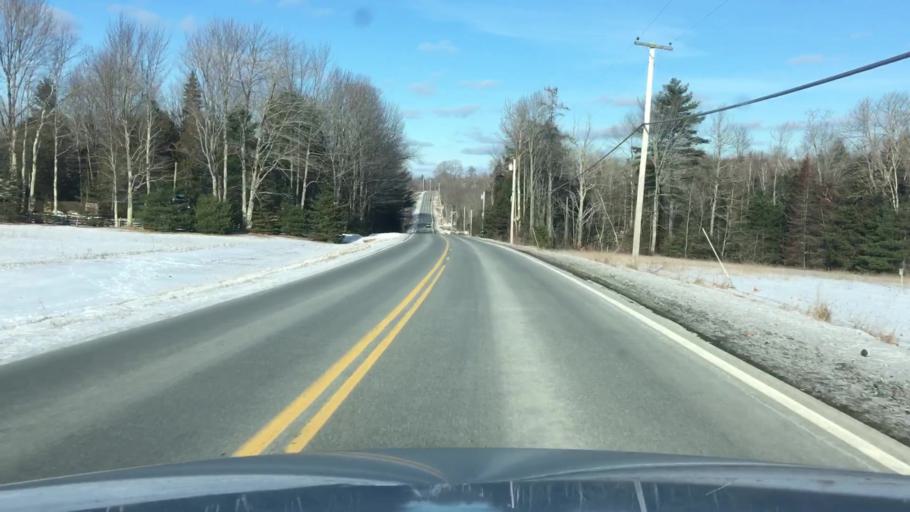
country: US
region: Maine
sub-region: Penobscot County
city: Holden
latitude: 44.7582
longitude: -68.5960
